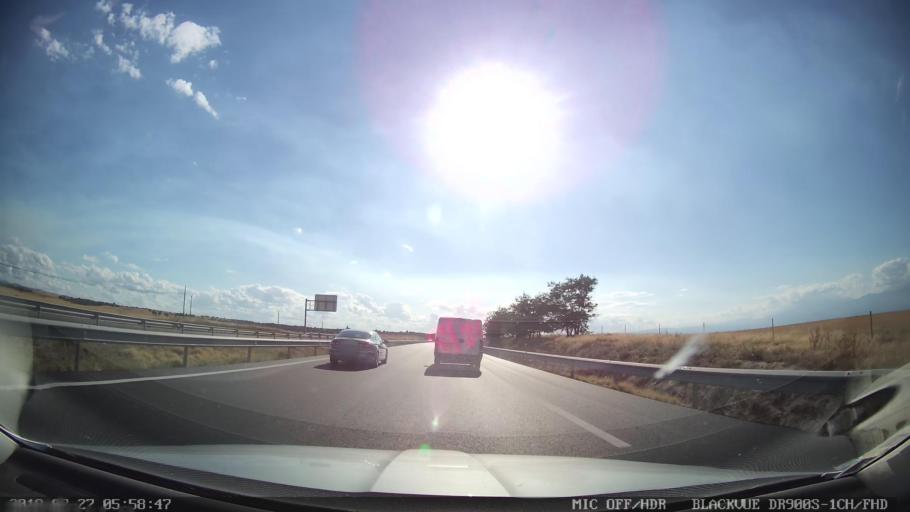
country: ES
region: Castille-La Mancha
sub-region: Province of Toledo
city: Herreruela de Oropesa
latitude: 39.9029
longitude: -5.2523
